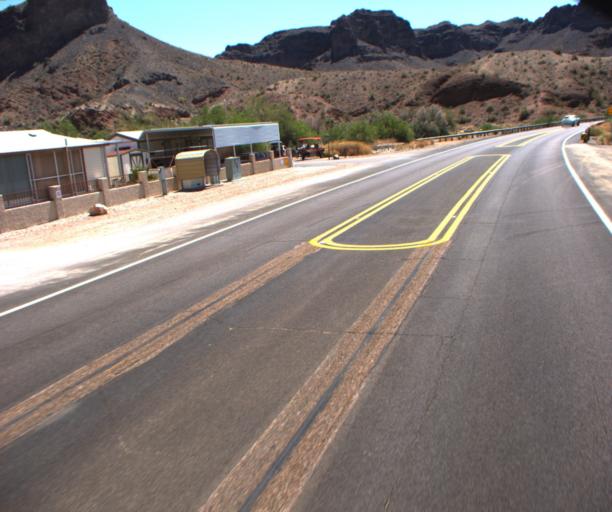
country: US
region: Arizona
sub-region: La Paz County
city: Cienega Springs
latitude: 34.2605
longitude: -114.1294
